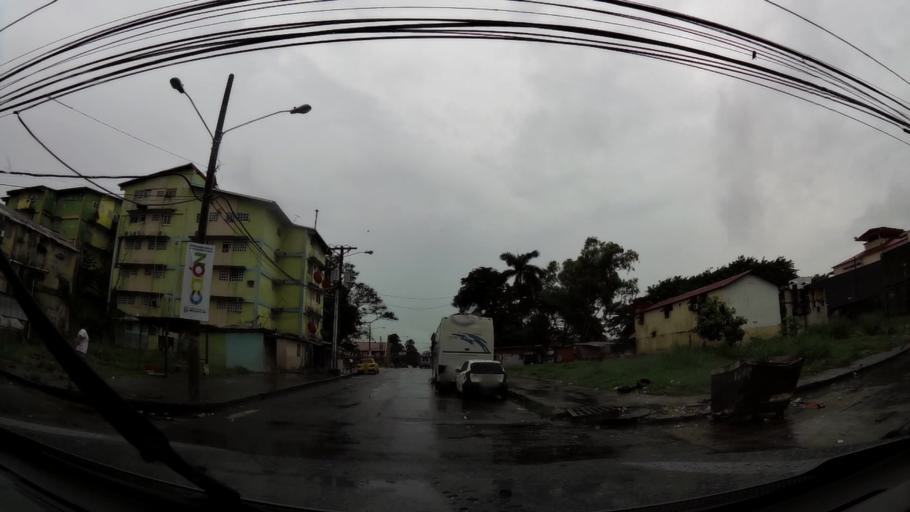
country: PA
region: Colon
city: Colon
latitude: 9.3604
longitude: -79.9031
